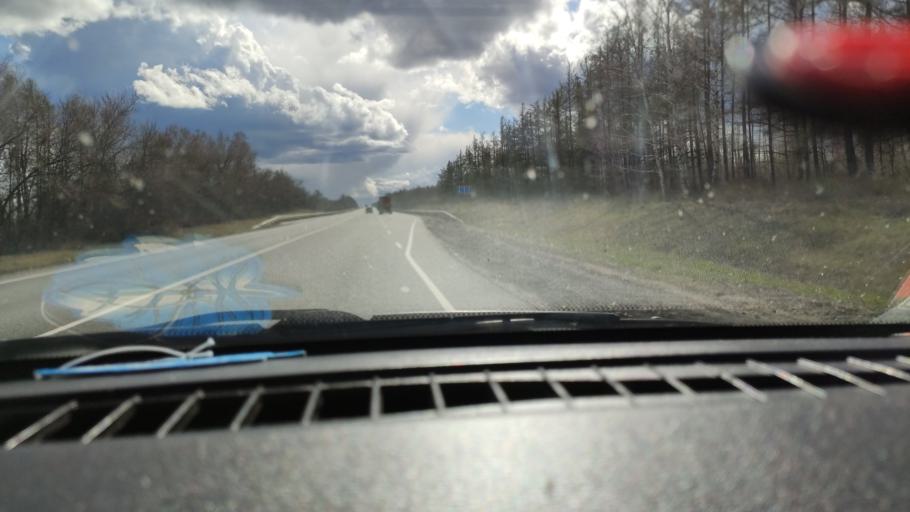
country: RU
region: Saratov
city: Khvalynsk
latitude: 52.5659
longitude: 48.0954
